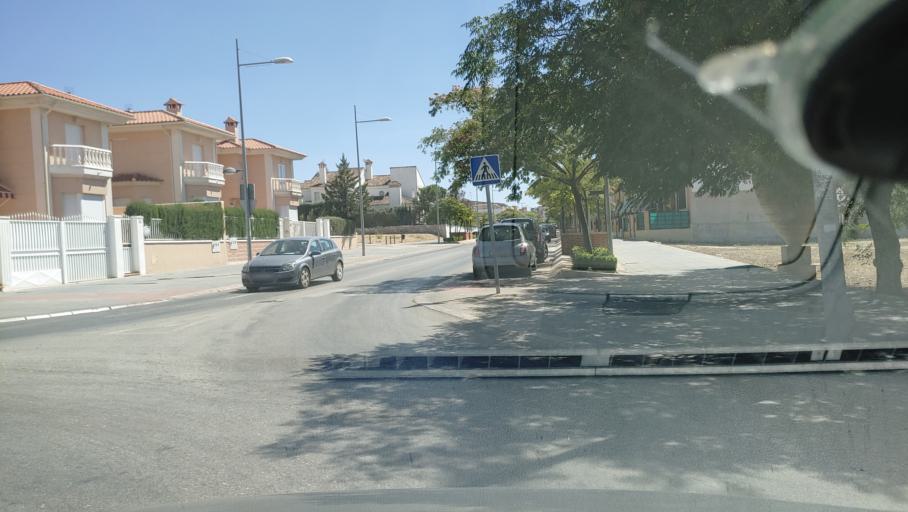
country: ES
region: Castille-La Mancha
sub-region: Provincia de Ciudad Real
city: Valdepenas
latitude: 38.7707
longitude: -3.3888
